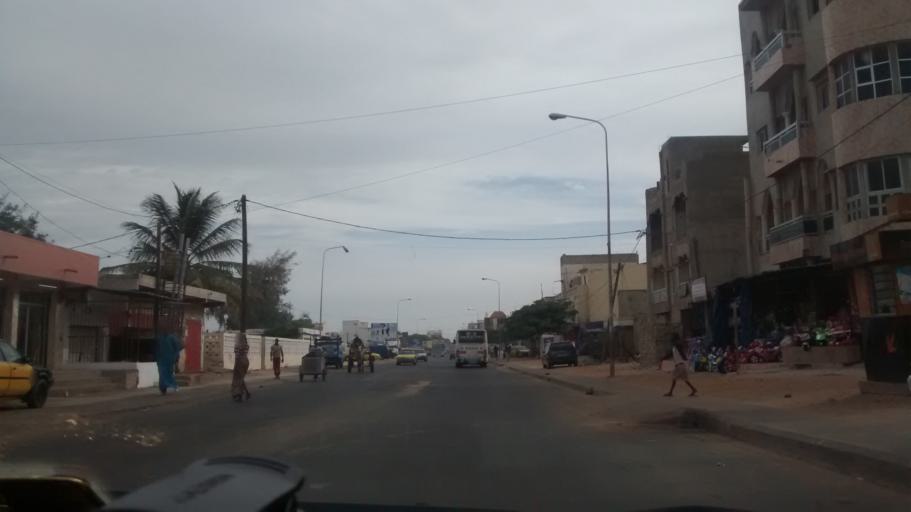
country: SN
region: Dakar
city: Pikine
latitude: 14.7806
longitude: -17.3891
